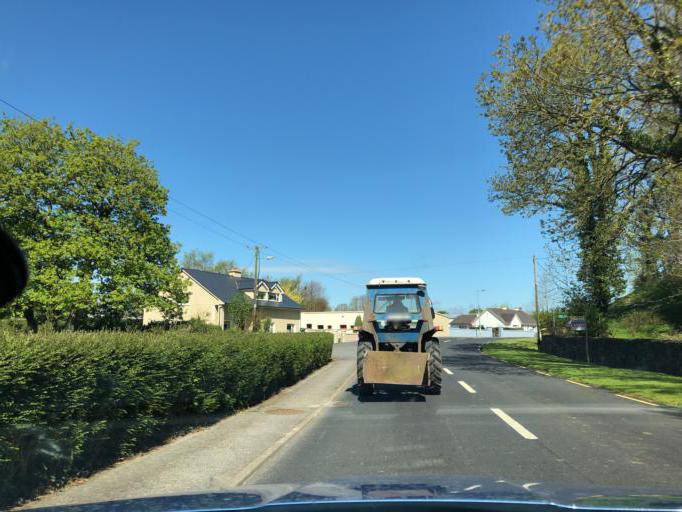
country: IE
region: Connaught
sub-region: County Galway
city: Portumna
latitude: 53.1467
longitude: -8.3716
